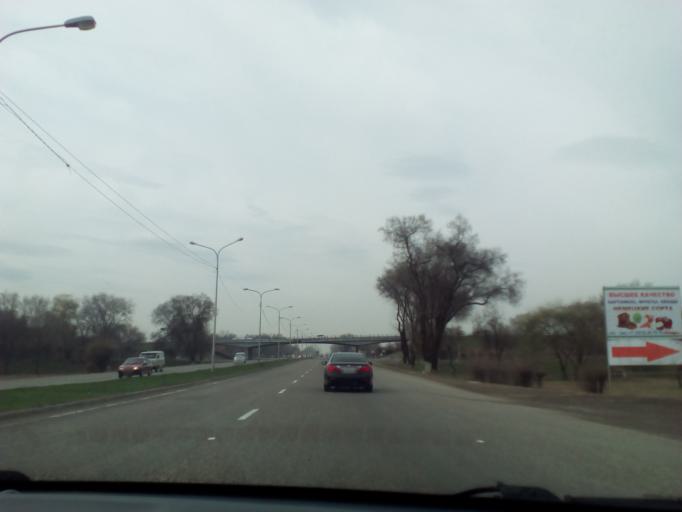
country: KZ
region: Almaty Oblysy
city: Burunday
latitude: 43.2178
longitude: 76.6518
